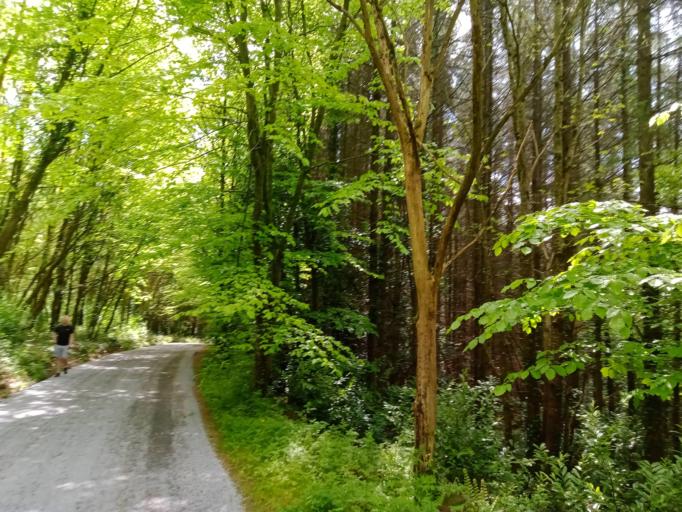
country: IE
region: Leinster
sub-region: Kilkenny
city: Castlecomer
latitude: 52.8124
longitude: -7.2019
